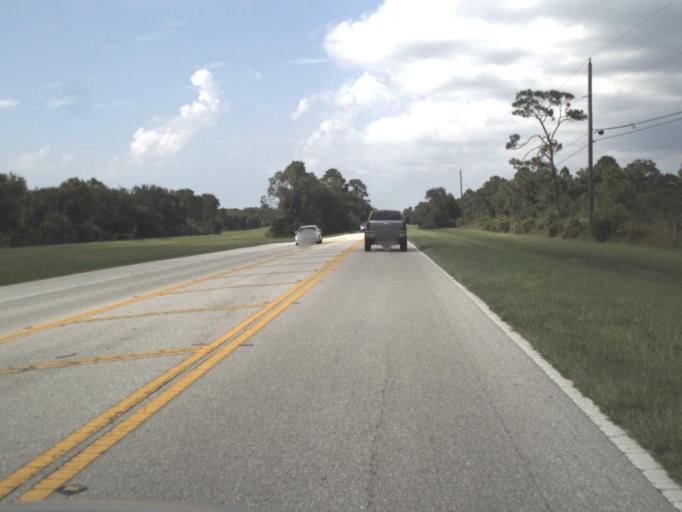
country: US
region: Florida
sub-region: Sarasota County
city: Plantation
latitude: 27.0852
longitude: -82.3345
